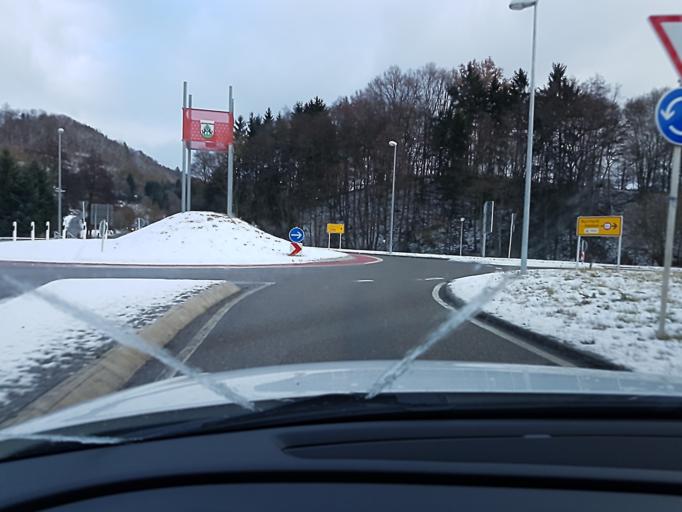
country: DE
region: Baden-Wuerttemberg
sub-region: Regierungsbezirk Stuttgart
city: Murrhardt
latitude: 48.9887
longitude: 9.5521
